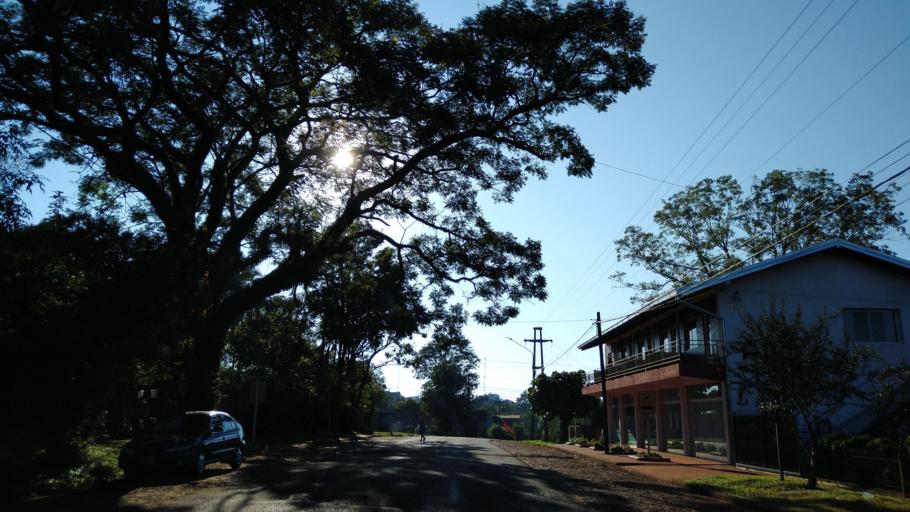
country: AR
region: Misiones
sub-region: Departamento de Montecarlo
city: Montecarlo
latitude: -26.5695
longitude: -54.7628
